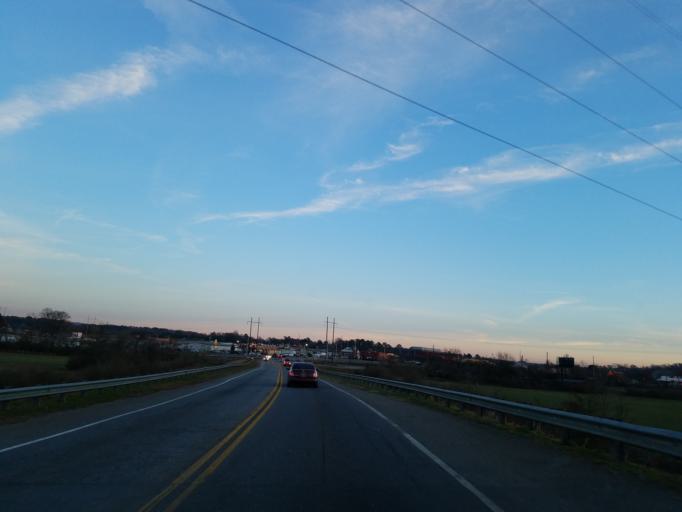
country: US
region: Georgia
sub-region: Bartow County
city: Cartersville
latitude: 34.1532
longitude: -84.8275
